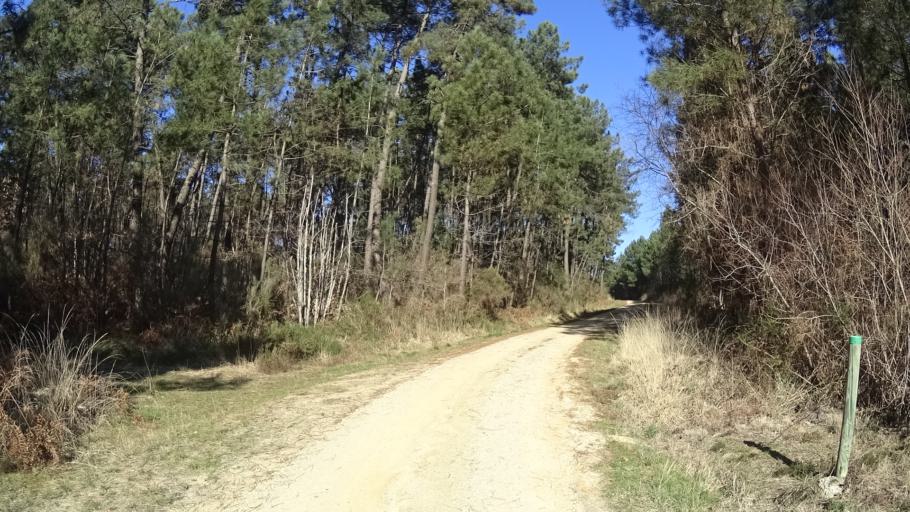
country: FR
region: Aquitaine
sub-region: Departement de la Dordogne
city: Montpon-Menesterol
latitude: 45.0520
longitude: 0.2404
